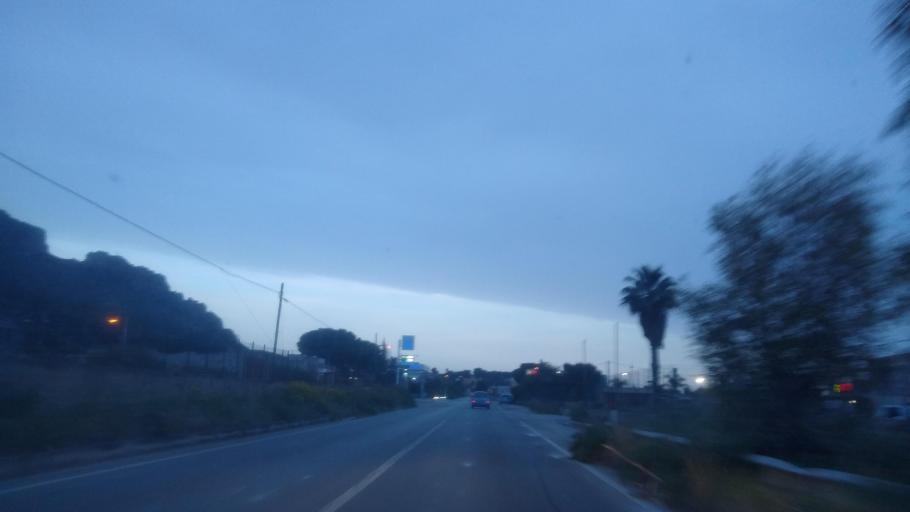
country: IT
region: Sicily
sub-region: Palermo
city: Terrasini
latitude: 38.1421
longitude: 13.0844
